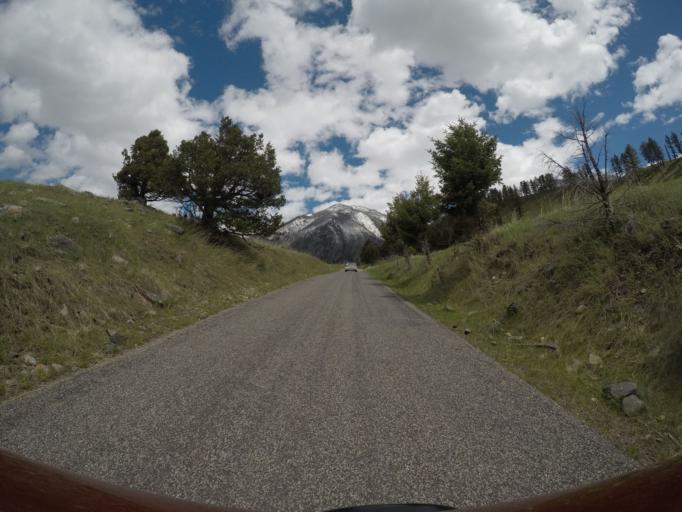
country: US
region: Montana
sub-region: Park County
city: Livingston
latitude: 45.4997
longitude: -110.5462
